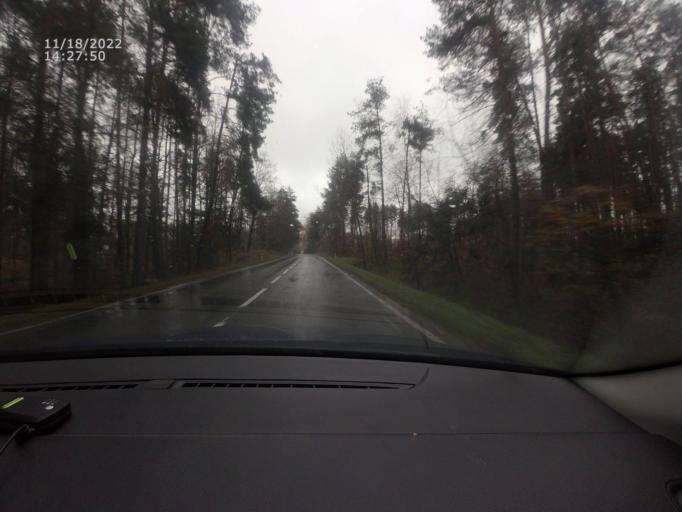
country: CZ
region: Jihocesky
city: Kovarov
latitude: 49.4232
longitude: 14.2053
